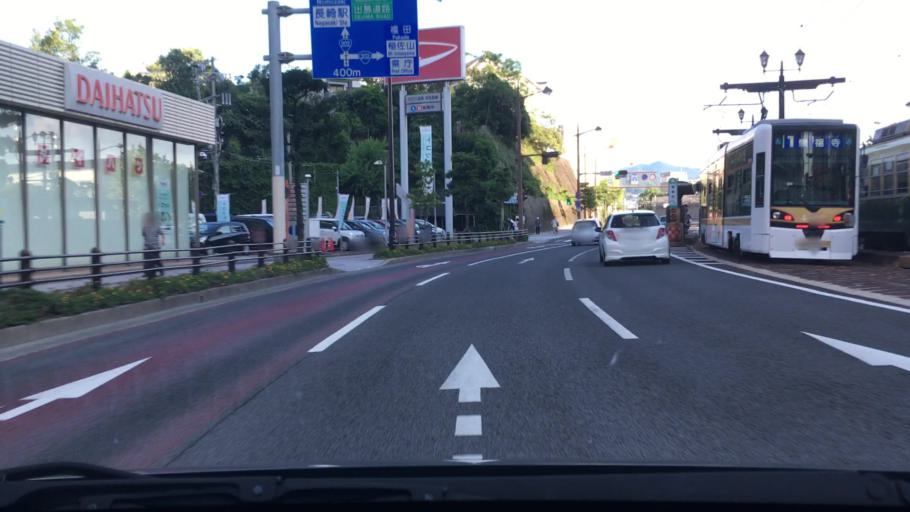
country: JP
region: Nagasaki
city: Nagasaki-shi
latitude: 32.7617
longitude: 129.8658
